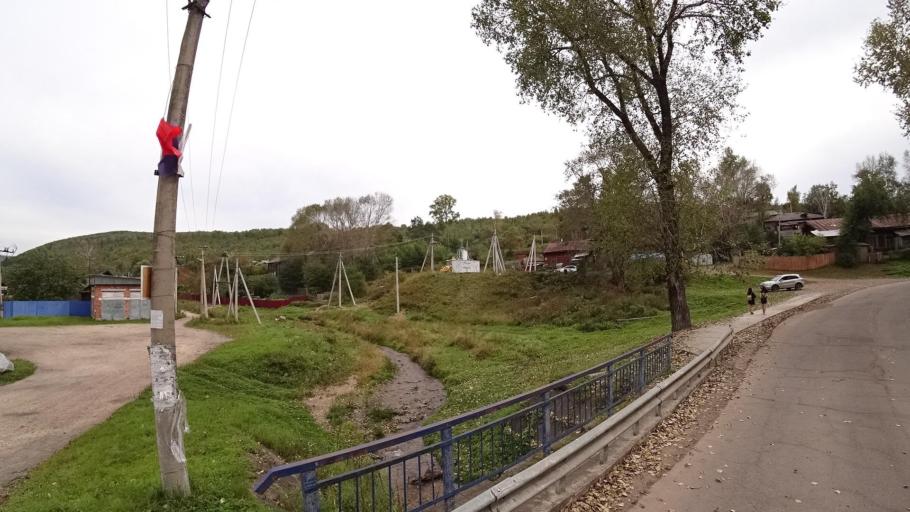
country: RU
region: Jewish Autonomous Oblast
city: Khingansk
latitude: 49.0193
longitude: 131.0630
